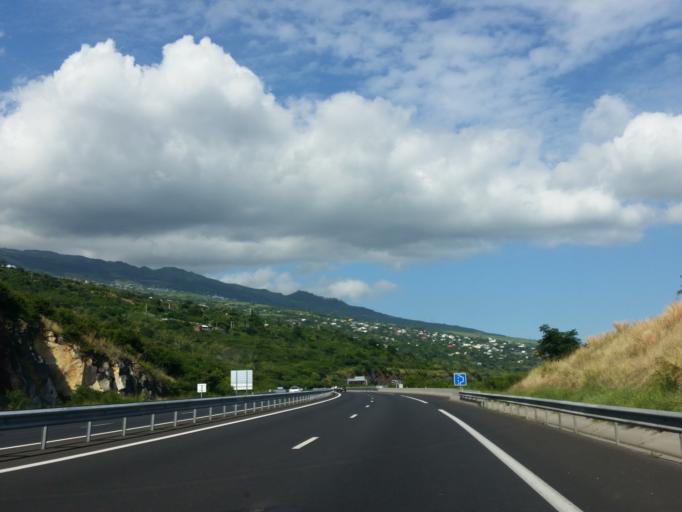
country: RE
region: Reunion
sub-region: Reunion
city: Saint-Leu
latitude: -21.1522
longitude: 55.2915
